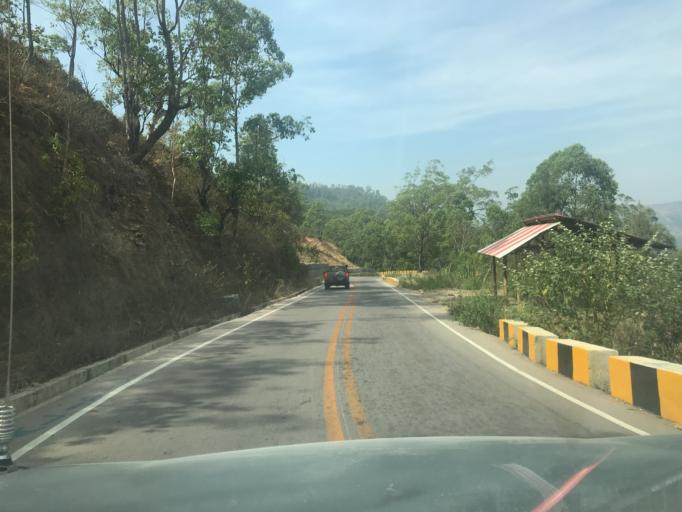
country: TL
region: Aileu
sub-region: Aileu Villa
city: Aileu
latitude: -8.6656
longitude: 125.5589
